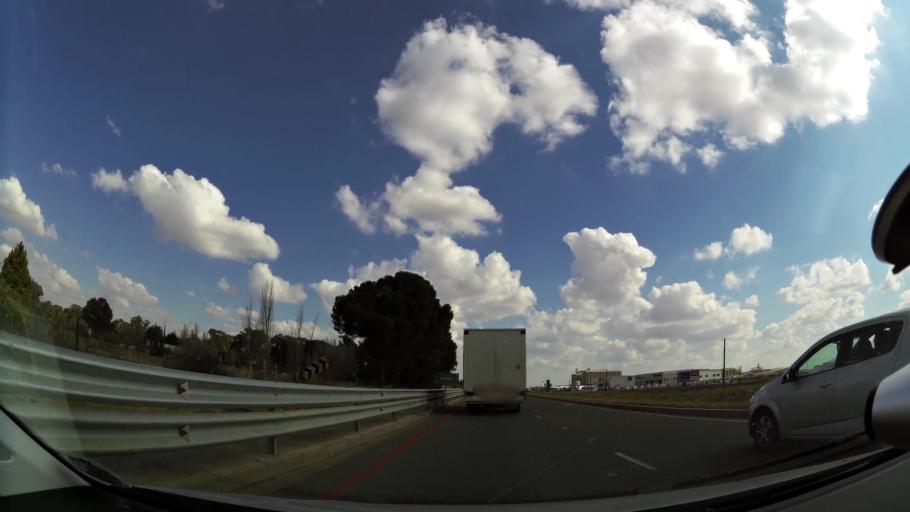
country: ZA
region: Orange Free State
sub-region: Mangaung Metropolitan Municipality
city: Bloemfontein
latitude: -29.1308
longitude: 26.1492
